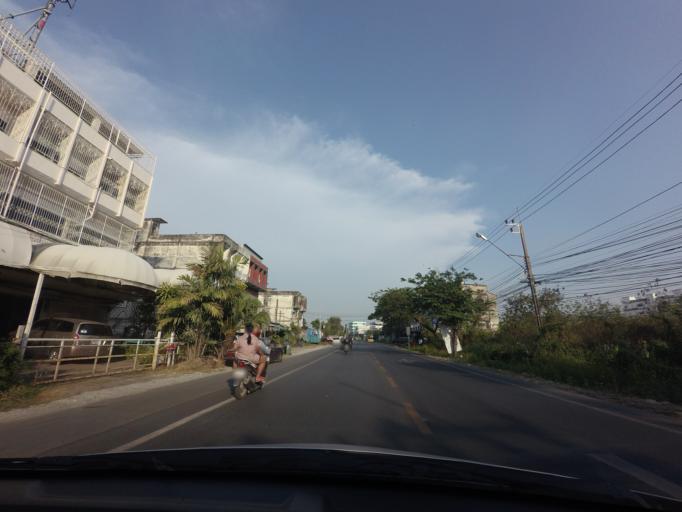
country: TH
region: Bangkok
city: Saphan Sung
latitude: 13.7413
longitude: 100.6830
